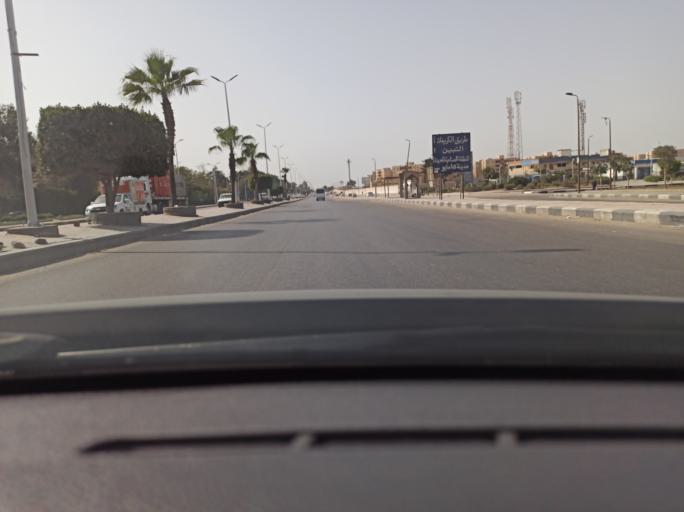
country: EG
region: Muhafazat al Qahirah
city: Halwan
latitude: 29.8317
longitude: 31.3554
